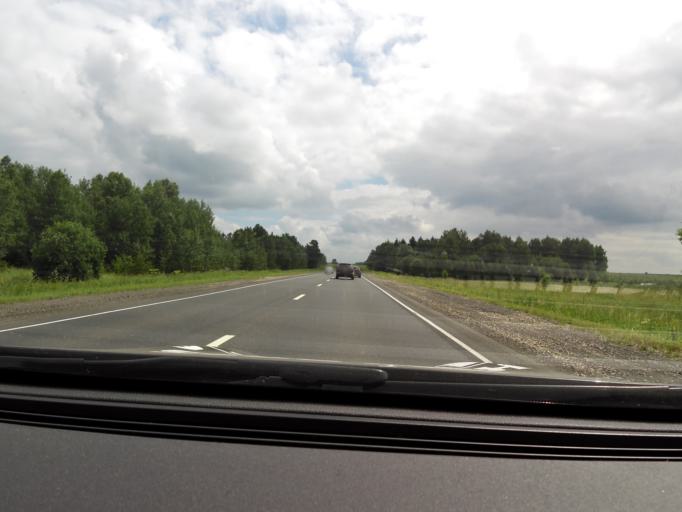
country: RU
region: Perm
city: Orda
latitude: 57.2510
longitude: 57.0399
